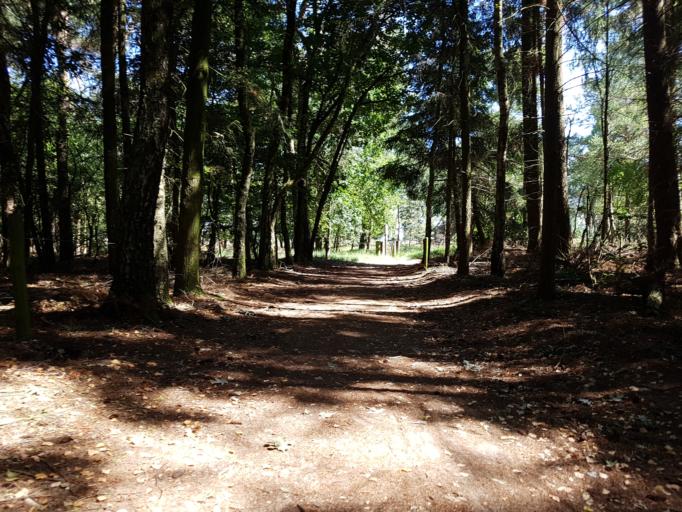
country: NL
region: North Brabant
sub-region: Gemeente Haaren
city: Haaren
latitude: 51.5790
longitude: 5.2478
